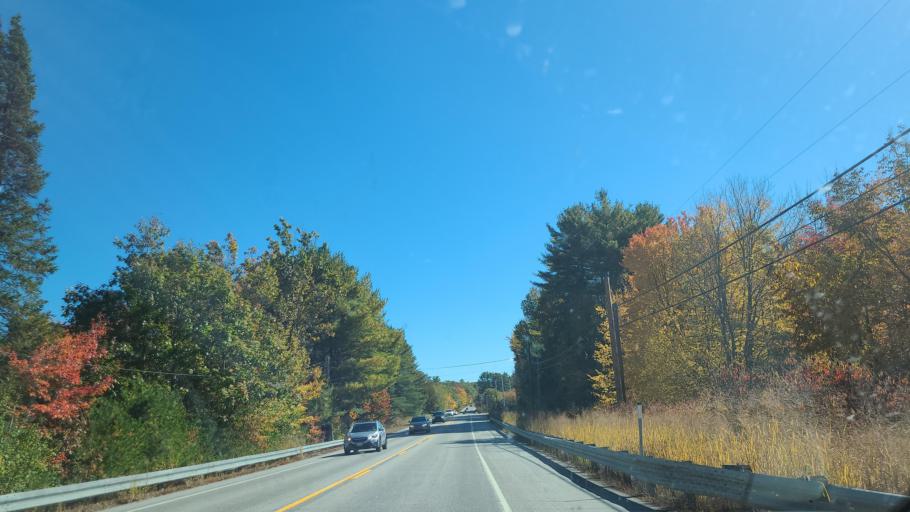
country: US
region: Maine
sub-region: Cumberland County
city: Bridgton
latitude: 44.0698
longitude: -70.7762
